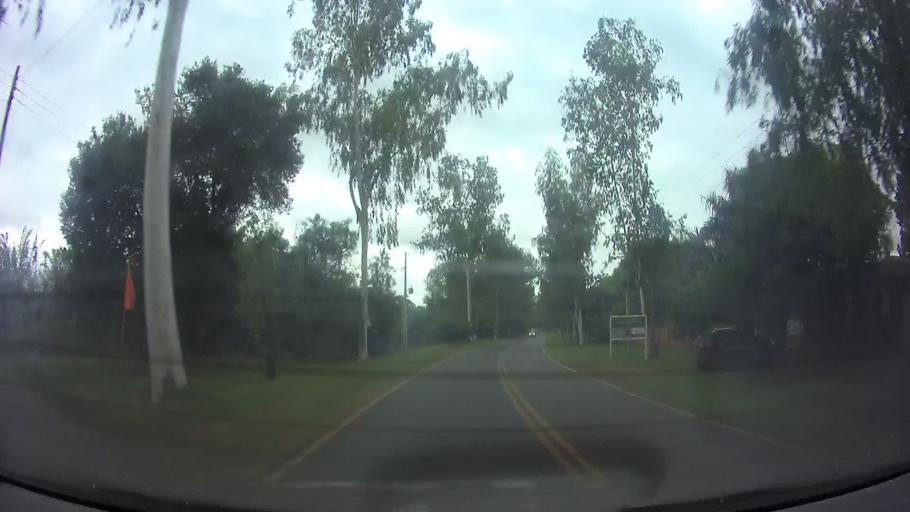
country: PY
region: Central
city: Nueva Italia
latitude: -25.5518
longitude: -57.5022
